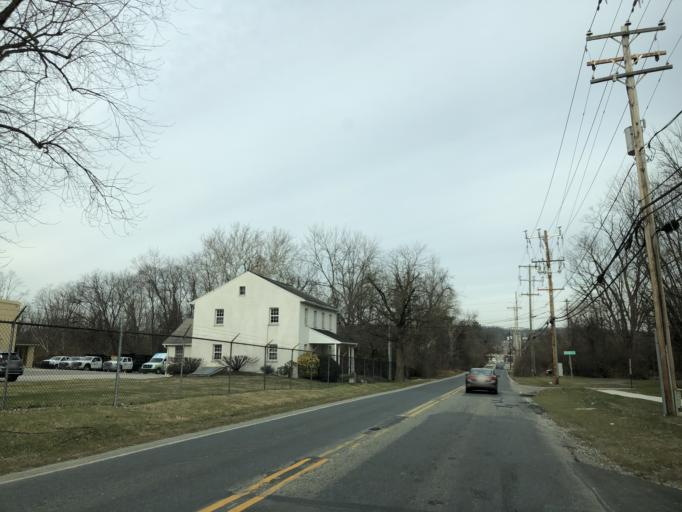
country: US
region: Pennsylvania
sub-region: Chester County
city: Exton
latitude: 40.0194
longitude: -75.6411
